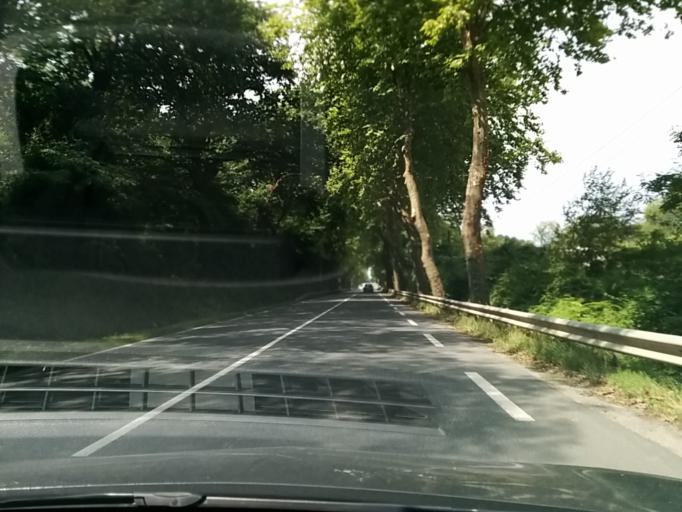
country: FR
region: Aquitaine
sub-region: Departement des Pyrenees-Atlantiques
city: Urrugne
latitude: 43.3613
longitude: -1.7203
